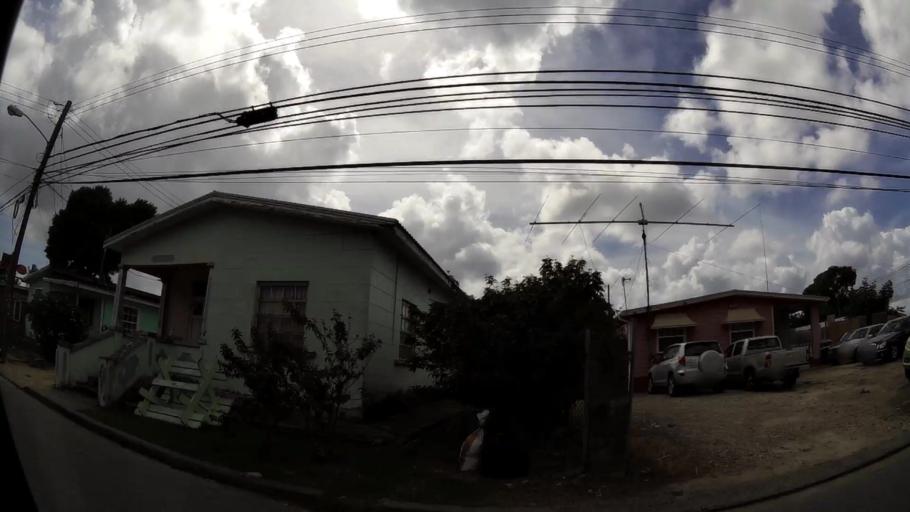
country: BB
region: Saint Michael
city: Bridgetown
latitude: 13.1242
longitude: -59.6085
